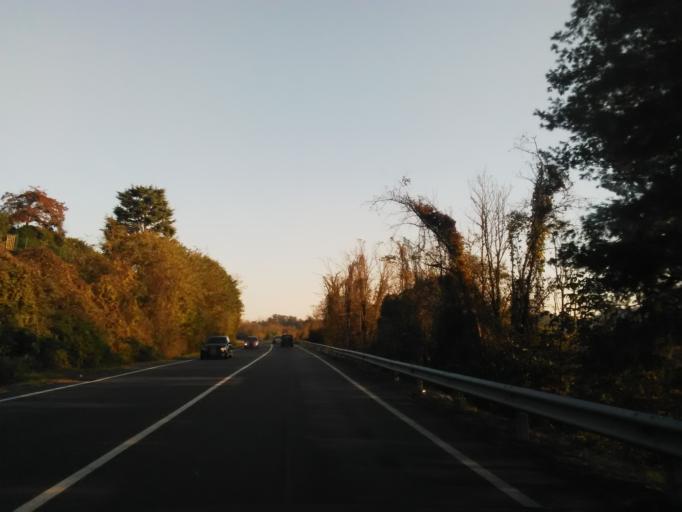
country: IT
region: Piedmont
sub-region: Provincia di Biella
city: Roppolo
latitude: 45.4146
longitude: 8.0685
